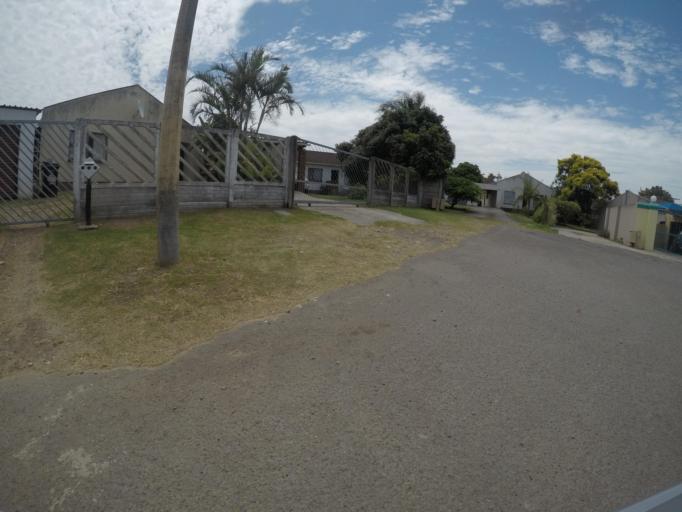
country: ZA
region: Eastern Cape
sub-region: Buffalo City Metropolitan Municipality
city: East London
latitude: -32.9801
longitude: 27.8605
